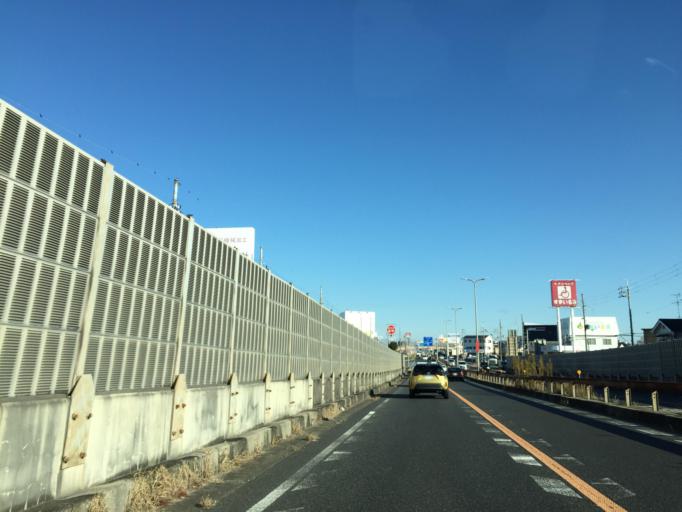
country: JP
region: Osaka
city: Kaizuka
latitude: 34.4167
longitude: 135.3367
